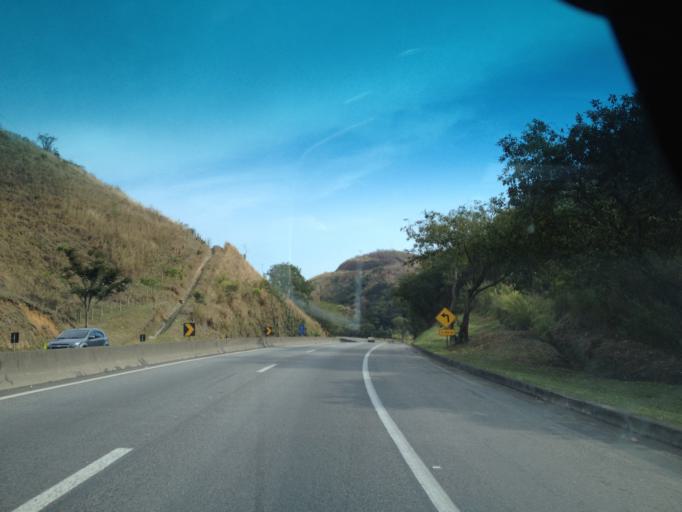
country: BR
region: Rio de Janeiro
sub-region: Barra Mansa
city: Barra Mansa
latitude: -22.5211
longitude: -44.2043
